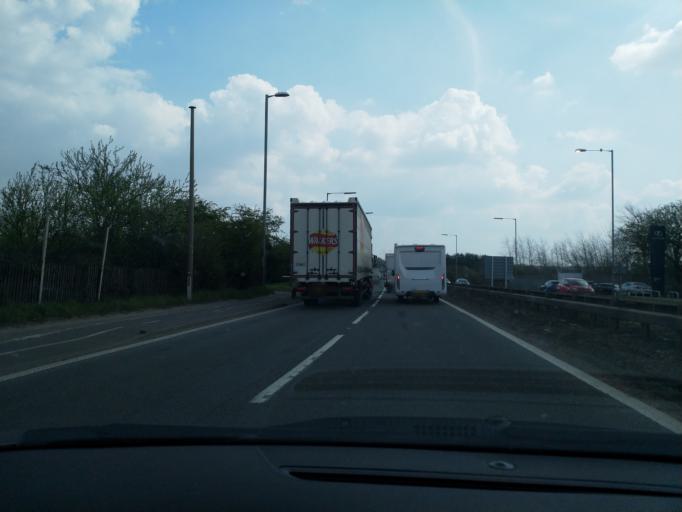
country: GB
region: England
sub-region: Warwickshire
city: Ryton on Dunsmore
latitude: 52.3770
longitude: -1.4636
